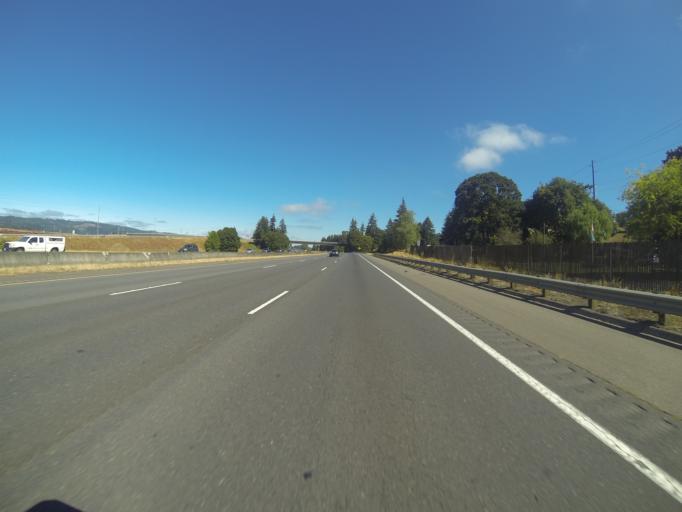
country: US
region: Washington
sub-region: Cowlitz County
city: Kalama
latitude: 46.0165
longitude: -122.8489
